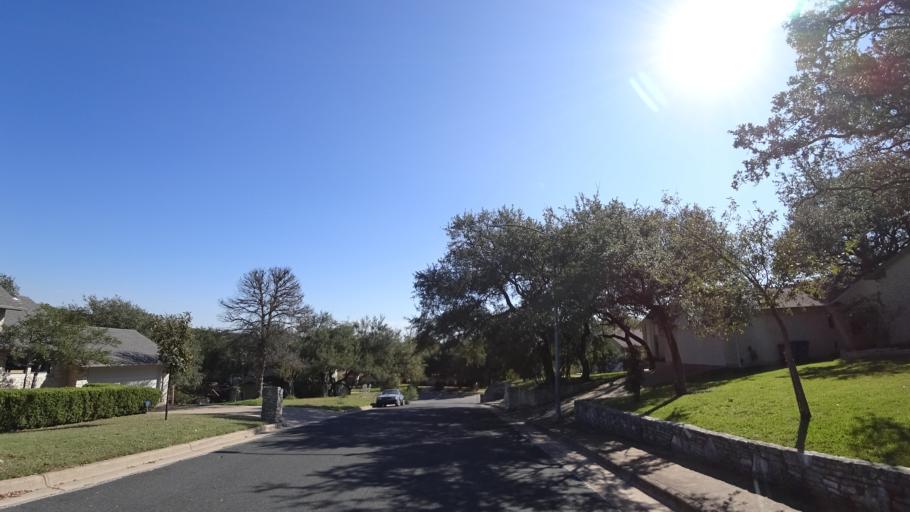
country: US
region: Texas
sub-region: Williamson County
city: Jollyville
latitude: 30.4202
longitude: -97.7646
